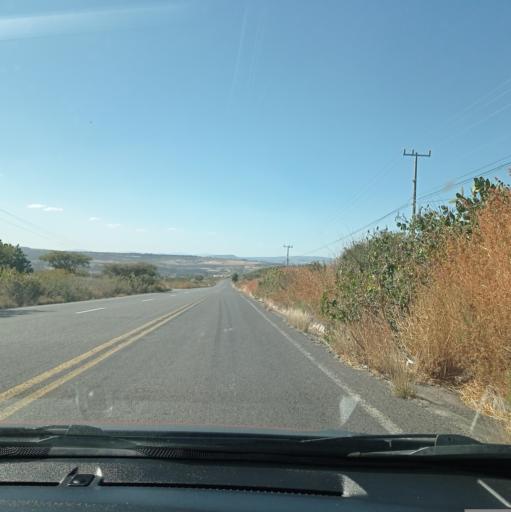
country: MX
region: Jalisco
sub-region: San Julian
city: Colonia Veintitres de Mayo
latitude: 21.0087
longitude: -102.2619
